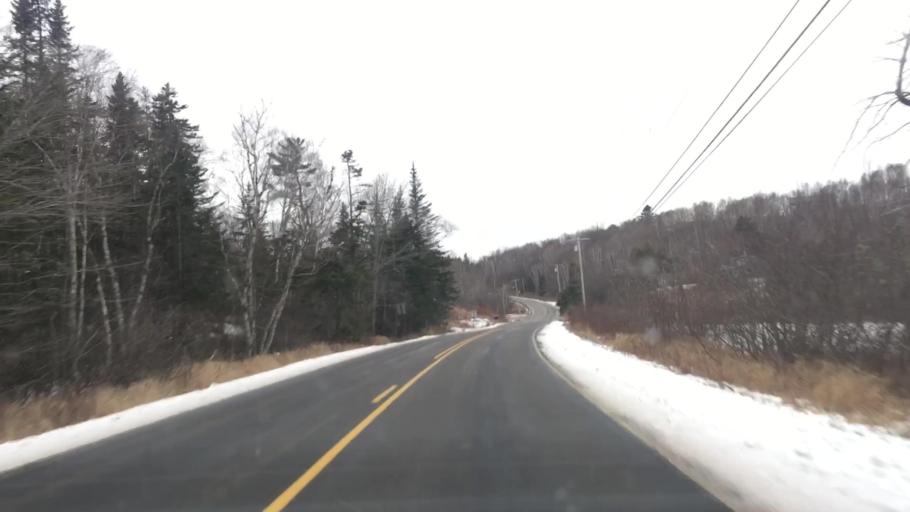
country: US
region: Maine
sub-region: Washington County
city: Machiasport
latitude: 44.7119
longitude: -67.3728
